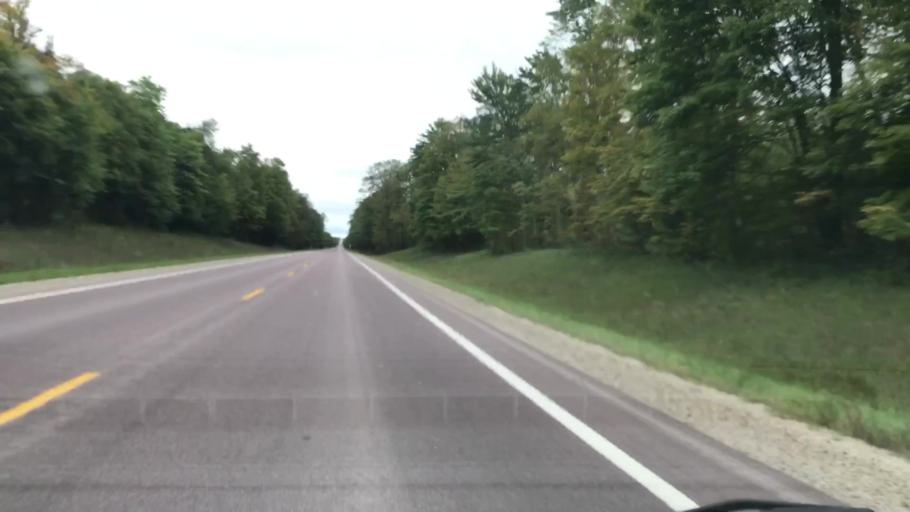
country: US
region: Michigan
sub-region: Luce County
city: Newberry
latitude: 46.2510
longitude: -85.5724
